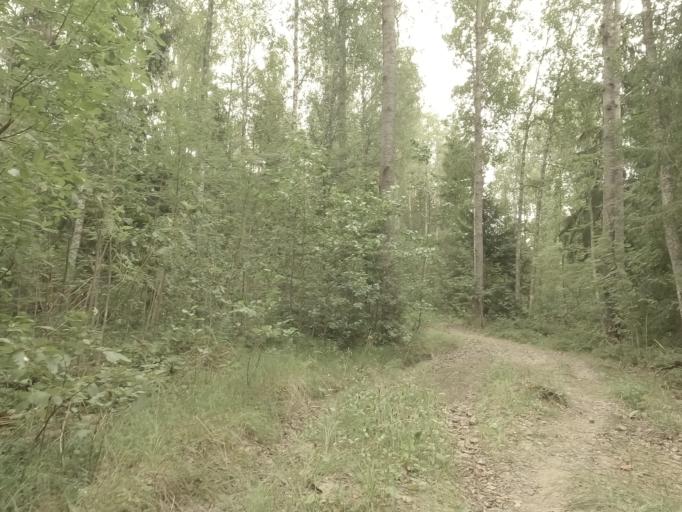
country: RU
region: Leningrad
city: Kamennogorsk
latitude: 61.0758
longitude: 29.1575
